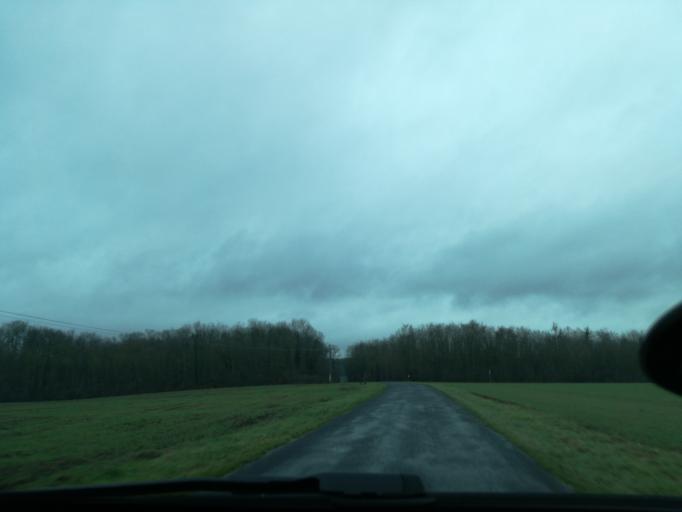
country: FR
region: Lorraine
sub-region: Departement de la Meuse
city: Revigny-sur-Ornain
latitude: 48.8486
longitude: 5.0564
